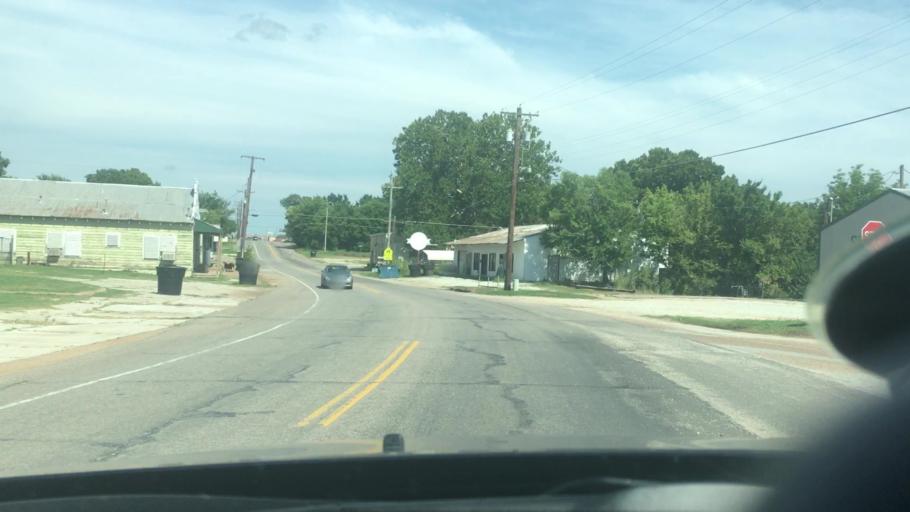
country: US
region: Oklahoma
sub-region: Seminole County
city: Seminole
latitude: 35.2249
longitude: -96.6790
